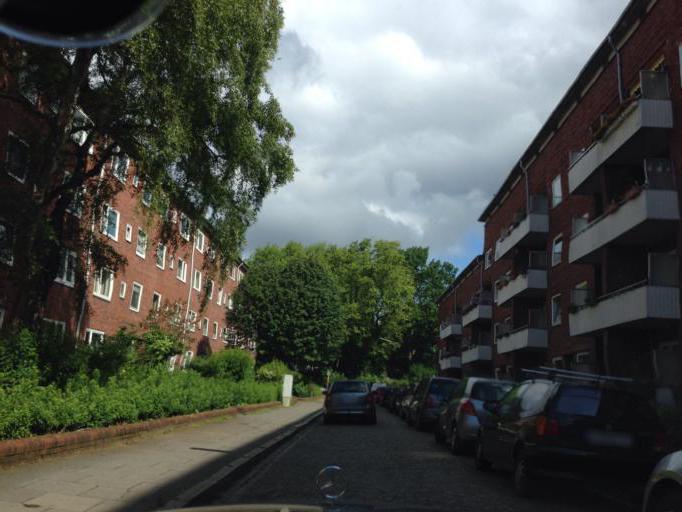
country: DE
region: Hamburg
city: Marienthal
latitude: 53.5850
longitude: 10.0713
